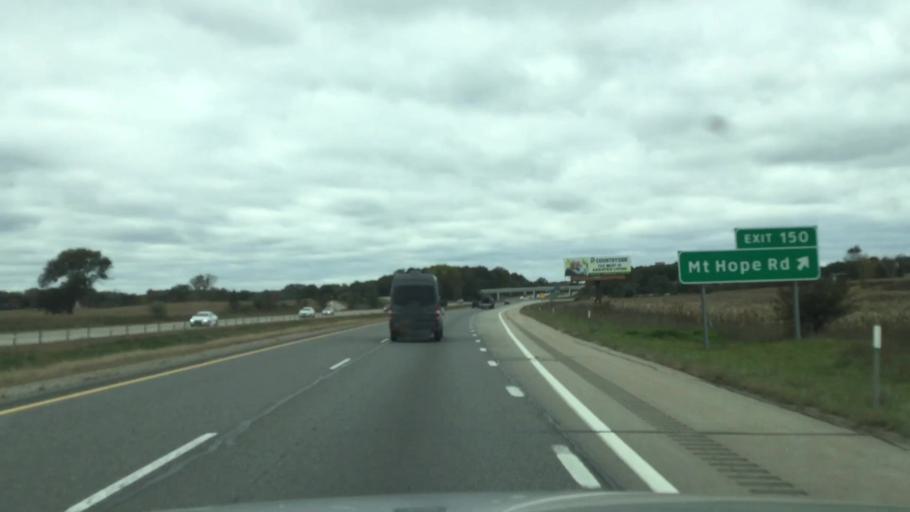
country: US
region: Michigan
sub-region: Jackson County
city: Grass Lake
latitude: 42.2905
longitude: -84.1973
